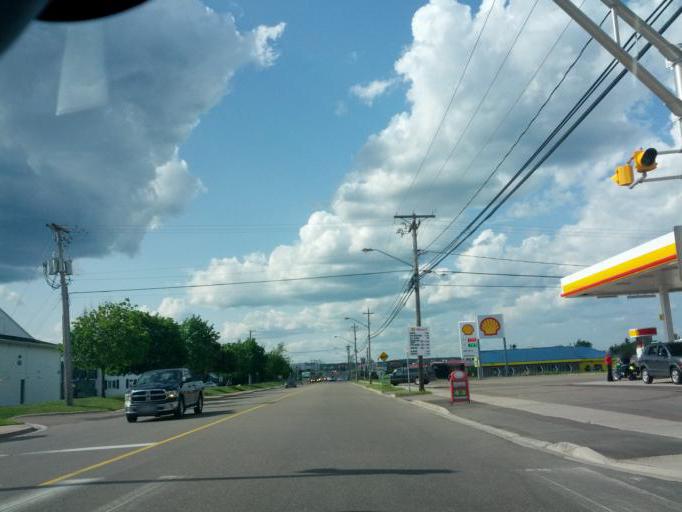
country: CA
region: New Brunswick
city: Moncton
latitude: 46.1111
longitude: -64.8242
